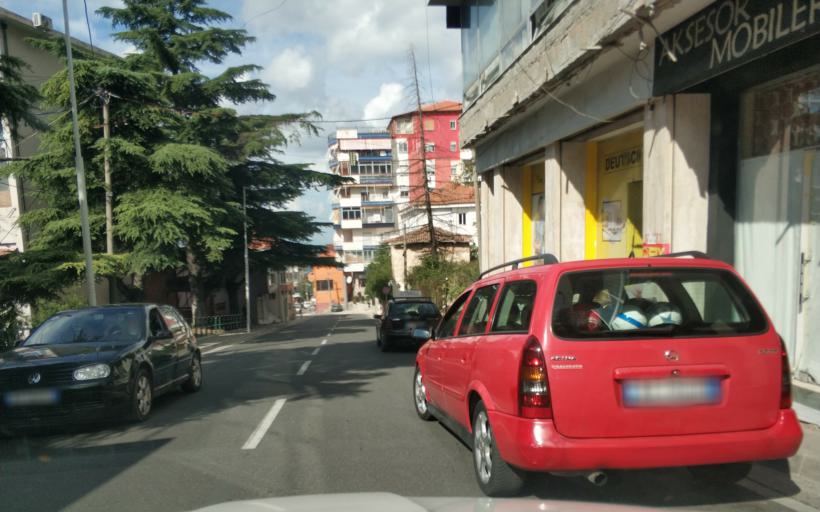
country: AL
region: Durres
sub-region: Rrethi i Krujes
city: Kruje
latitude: 41.5134
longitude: 19.7906
